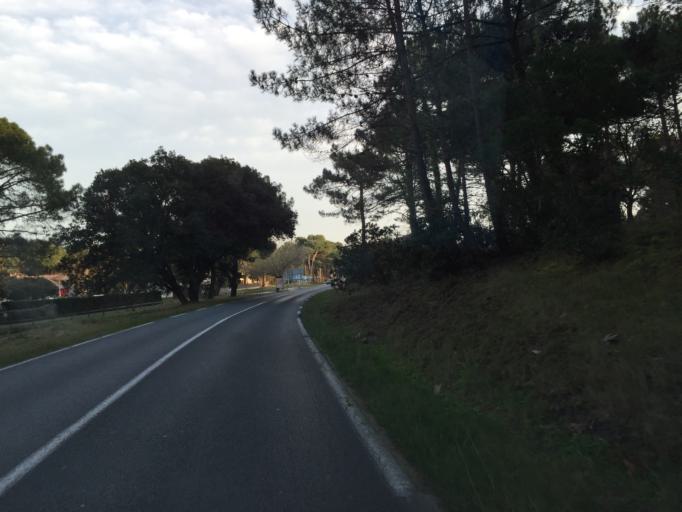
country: FR
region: Aquitaine
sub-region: Departement de la Gironde
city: Lacanau
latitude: 45.0060
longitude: -1.1736
